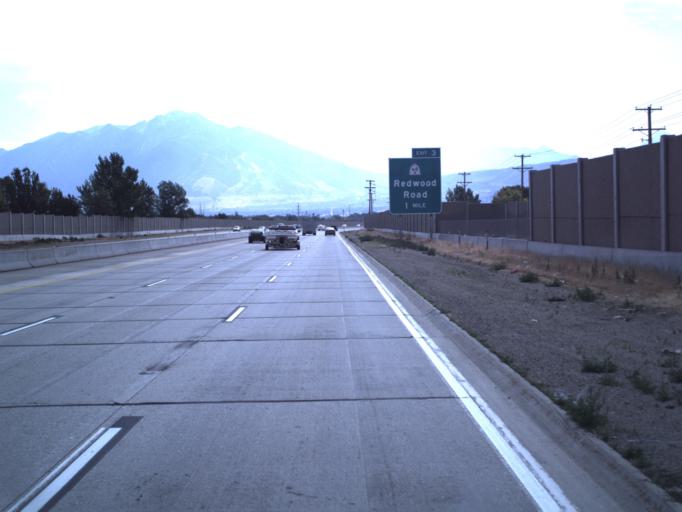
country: US
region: Utah
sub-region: Salt Lake County
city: Bluffdale
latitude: 40.5007
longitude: -111.9675
